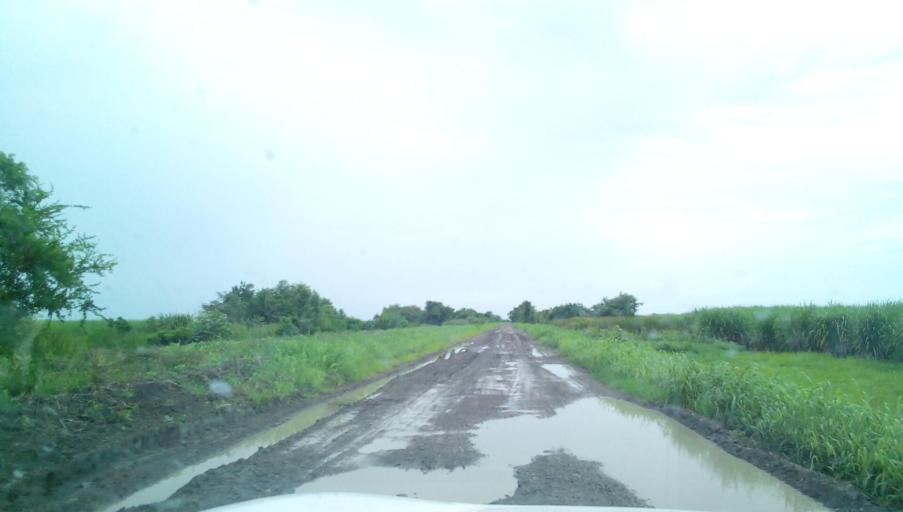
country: MX
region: Veracruz
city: Panuco
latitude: 21.8296
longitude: -98.1106
